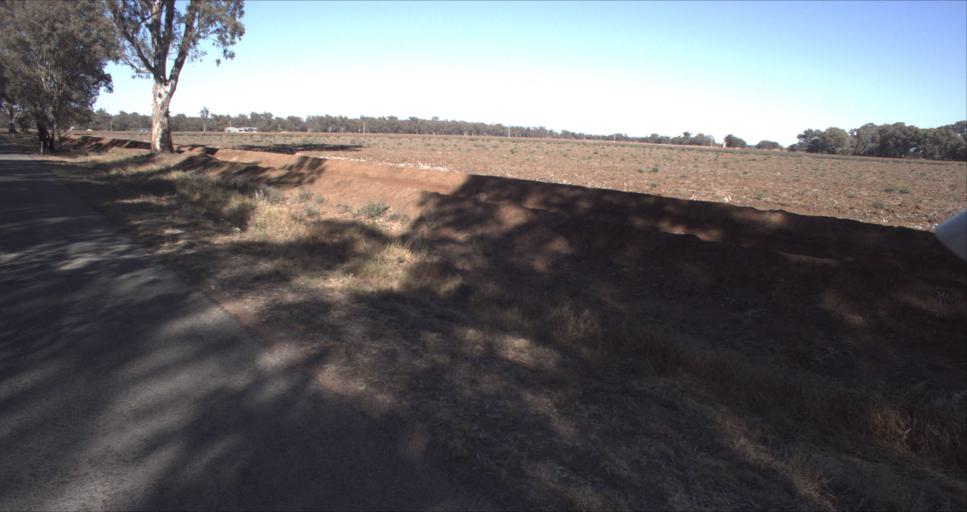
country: AU
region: New South Wales
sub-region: Leeton
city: Leeton
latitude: -34.6082
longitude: 146.2621
